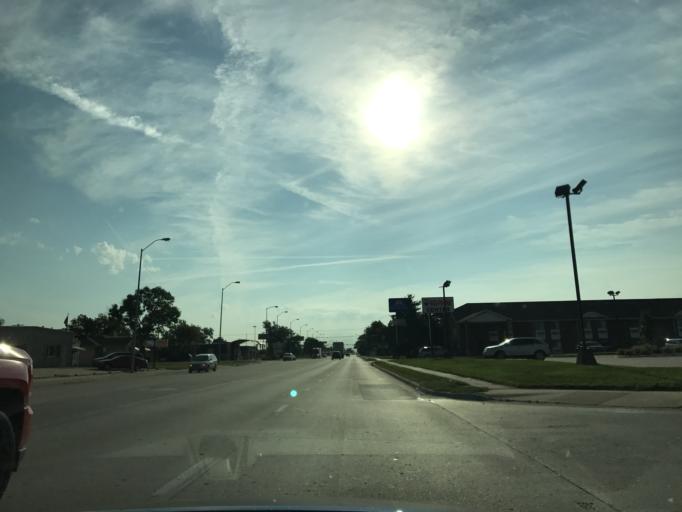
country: US
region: Nebraska
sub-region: Platte County
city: Columbus
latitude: 41.4387
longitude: -97.3758
